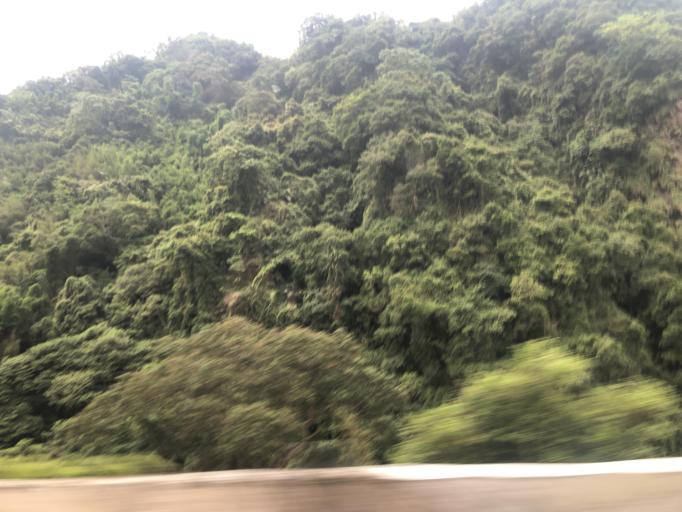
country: TW
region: Taiwan
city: Daxi
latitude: 24.8738
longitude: 121.3924
